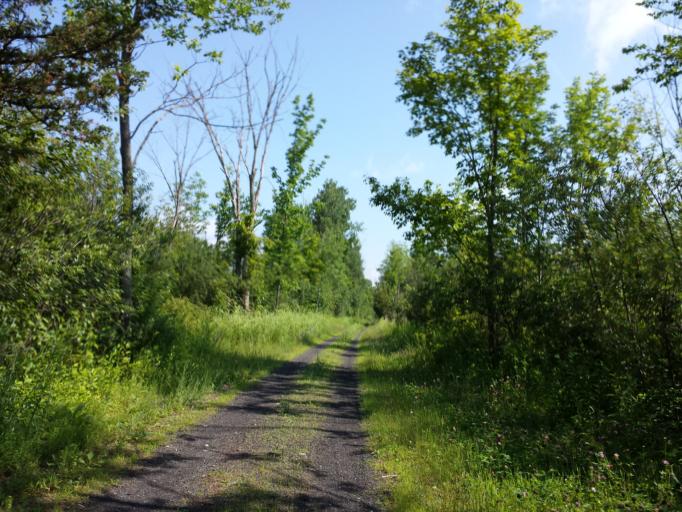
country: US
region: Vermont
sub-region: Rutland County
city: Poultney
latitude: 43.5370
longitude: -73.2330
